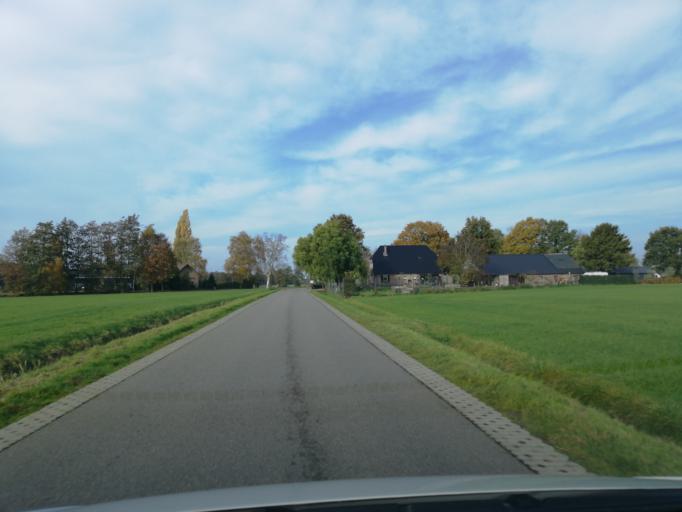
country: NL
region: Gelderland
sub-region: Gemeente Apeldoorn
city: Apeldoorn
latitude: 52.2473
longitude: 6.0165
